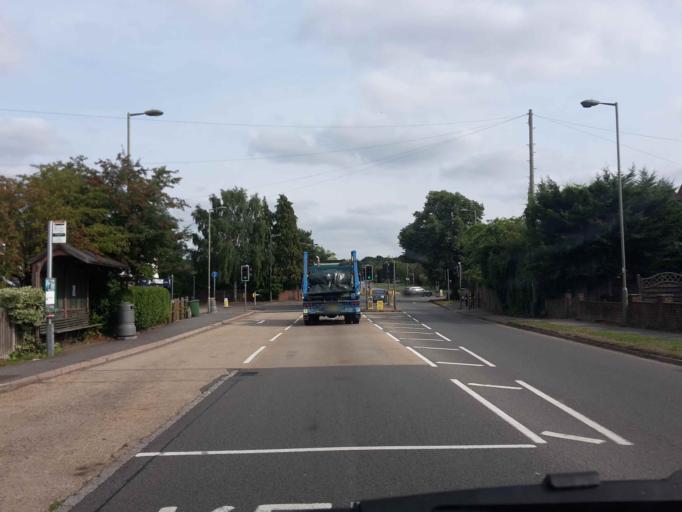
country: GB
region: England
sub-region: Surrey
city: Knaphill
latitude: 51.3234
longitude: -0.6345
